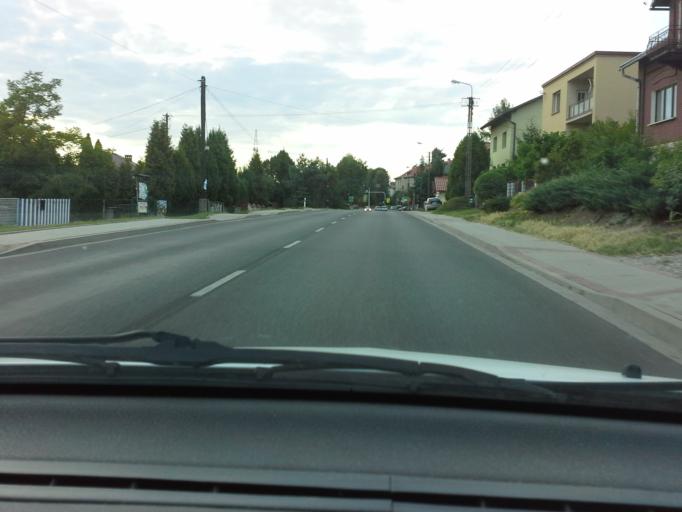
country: PL
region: Lesser Poland Voivodeship
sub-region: Powiat chrzanowski
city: Trzebinia
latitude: 50.1550
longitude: 19.4820
